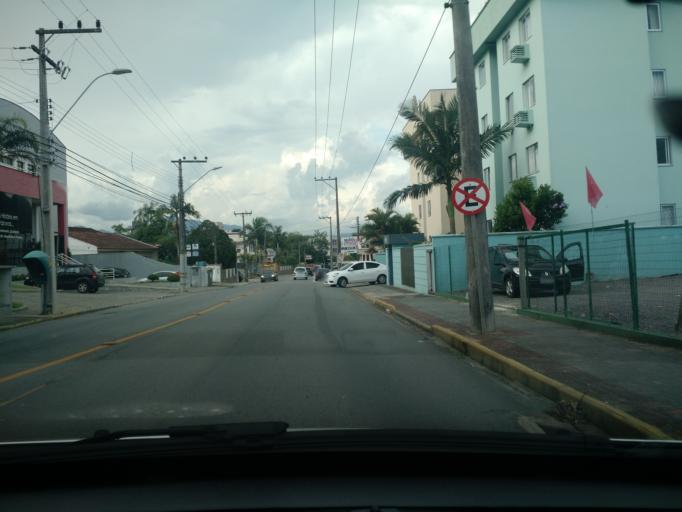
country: BR
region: Santa Catarina
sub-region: Jaragua Do Sul
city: Jaragua do Sul
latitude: -26.4883
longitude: -49.0919
